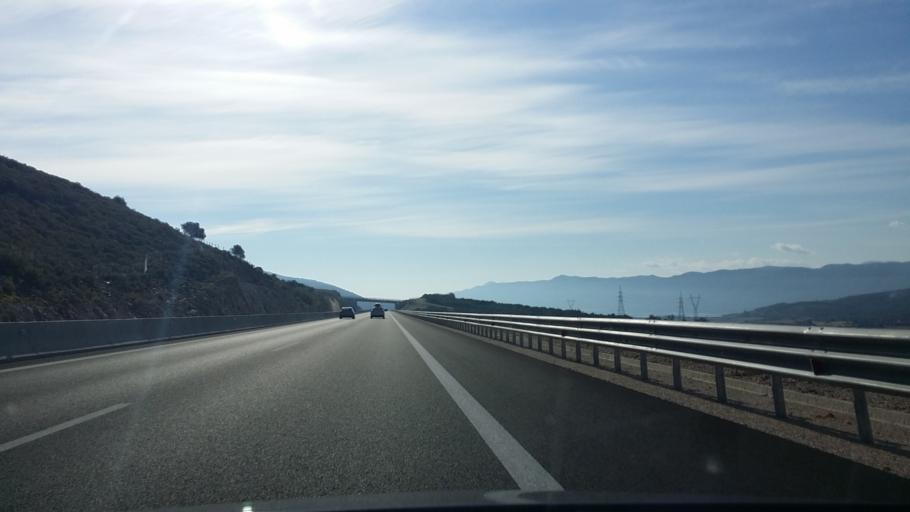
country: GR
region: West Greece
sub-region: Nomos Aitolias kai Akarnanias
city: Stanos
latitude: 38.8036
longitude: 21.1953
